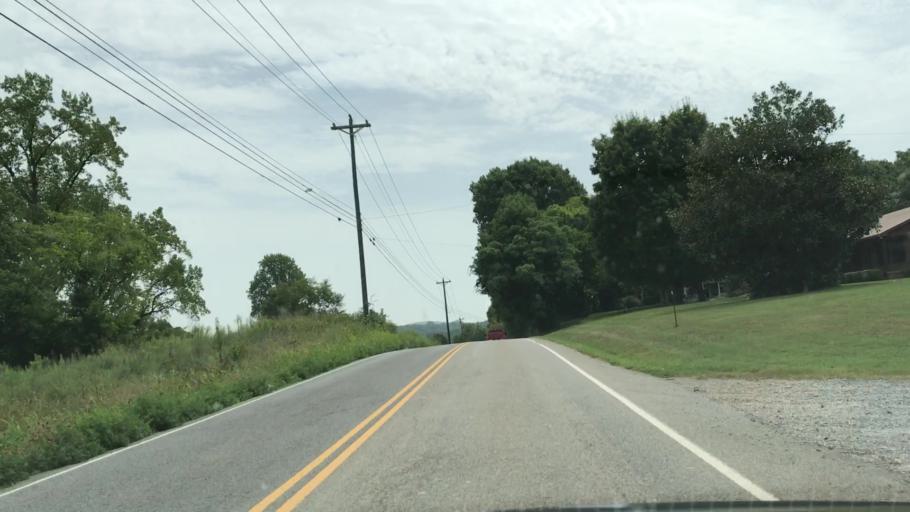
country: US
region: Tennessee
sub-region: Williamson County
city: Nolensville
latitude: 35.9370
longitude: -86.6980
